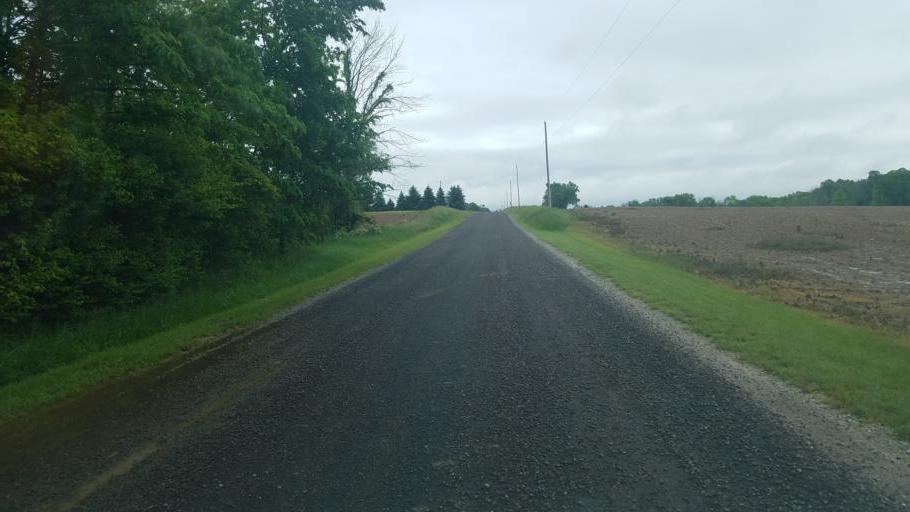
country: US
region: Ohio
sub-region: Morrow County
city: Mount Gilead
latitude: 40.5137
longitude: -82.7088
